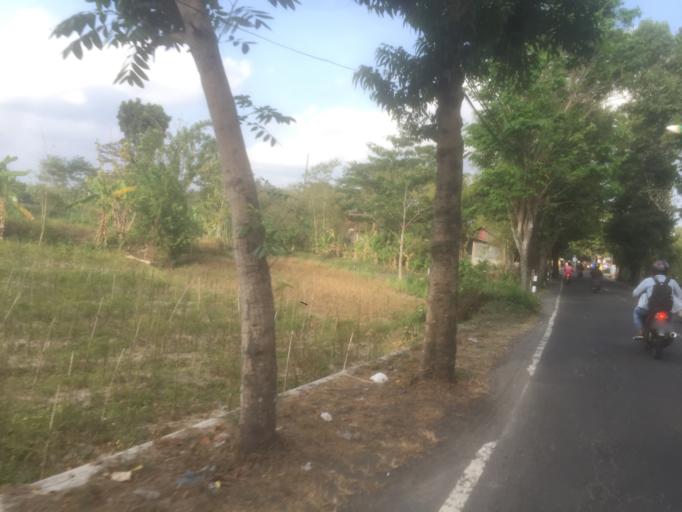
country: ID
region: Daerah Istimewa Yogyakarta
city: Melati
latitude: -7.7207
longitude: 110.3796
